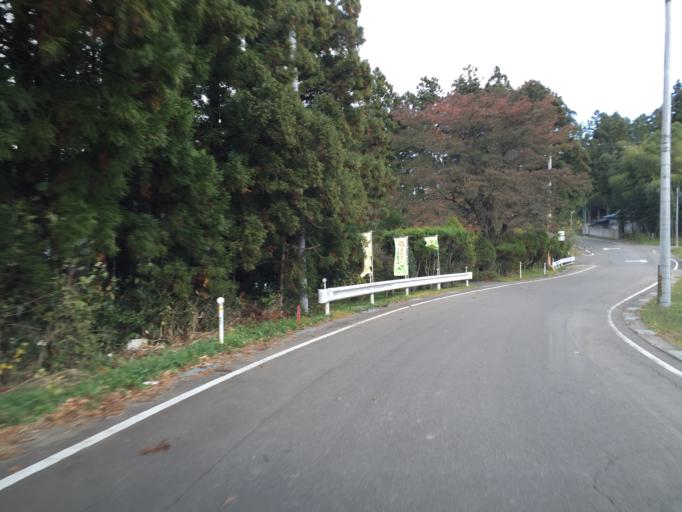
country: JP
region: Fukushima
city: Fukushima-shi
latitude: 37.7150
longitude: 140.3503
